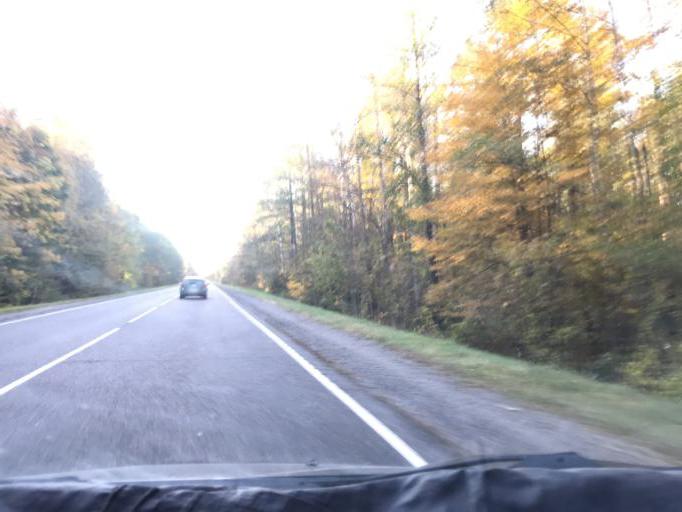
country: BY
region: Gomel
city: Pyetrykaw
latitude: 52.2680
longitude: 28.2908
